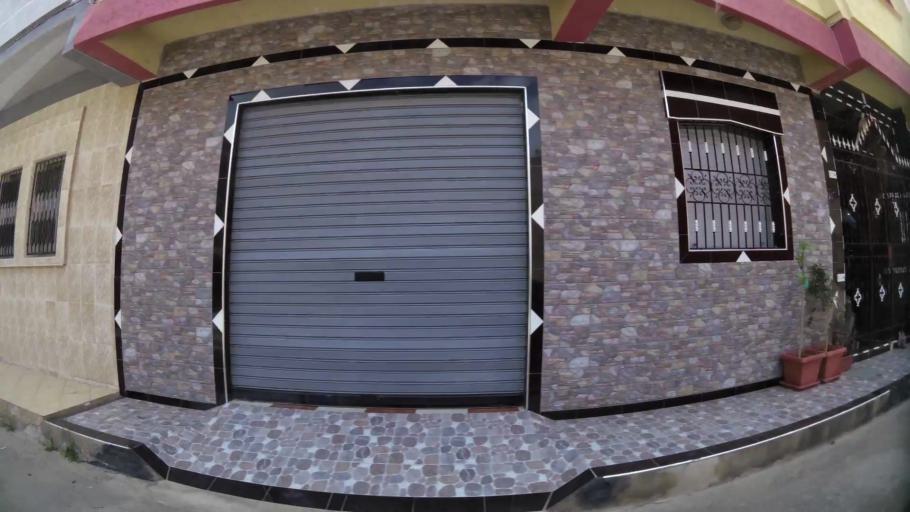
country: MA
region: Oriental
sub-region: Nador
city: Nador
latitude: 35.1645
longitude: -2.9223
